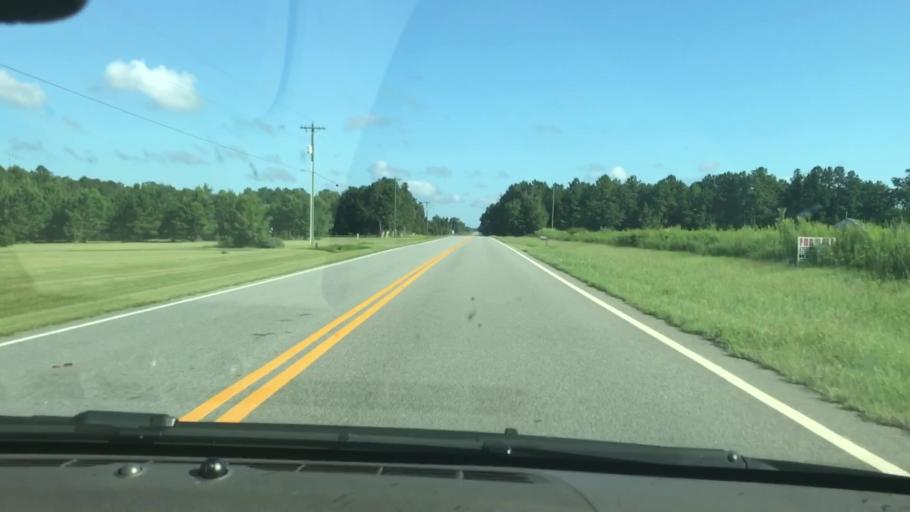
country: US
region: Georgia
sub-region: Quitman County
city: Georgetown
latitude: 31.7867
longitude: -85.0918
